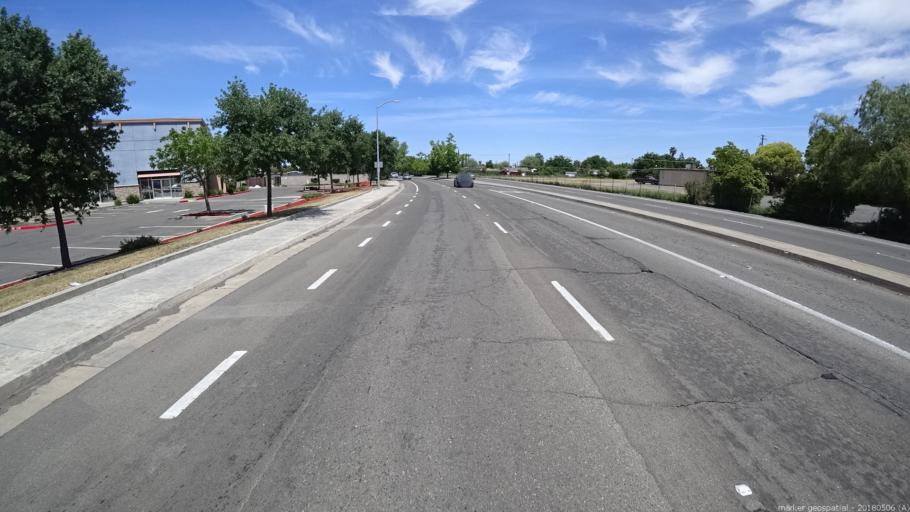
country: US
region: California
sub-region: Sacramento County
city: Florin
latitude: 38.5027
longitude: -121.4283
